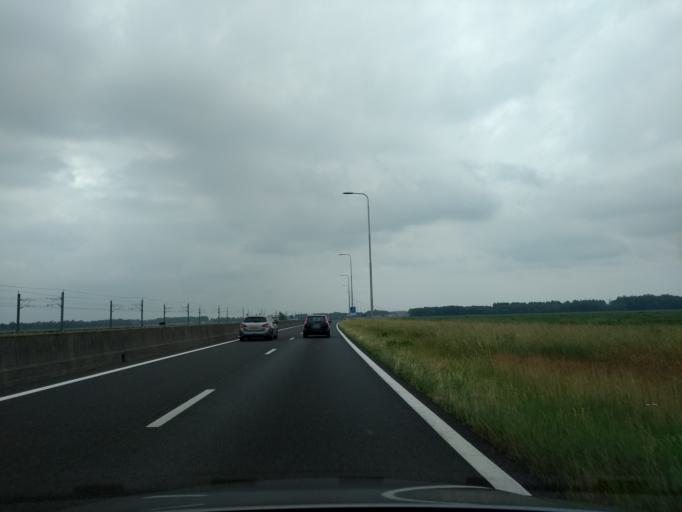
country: NL
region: Gelderland
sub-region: Gemeente Hattem
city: Hattem
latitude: 52.4979
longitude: 6.0068
